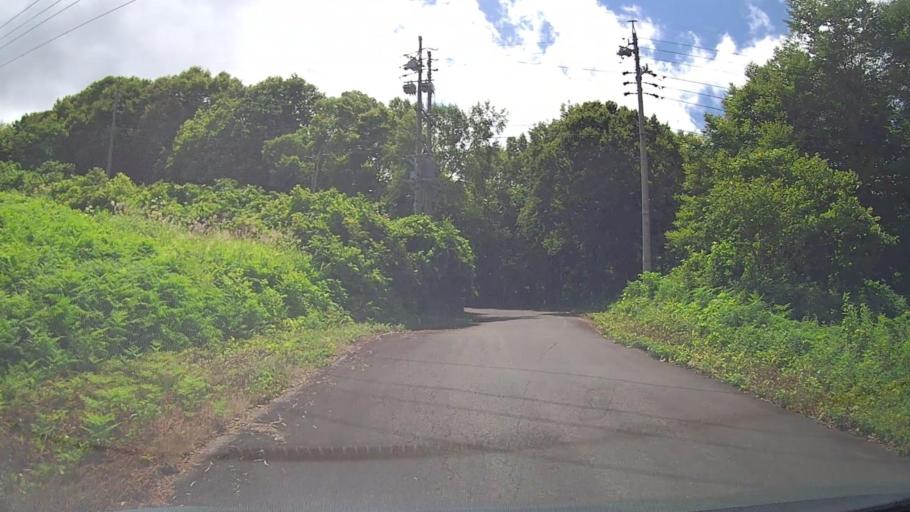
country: JP
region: Nagano
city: Iiyama
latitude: 36.9226
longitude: 138.4753
